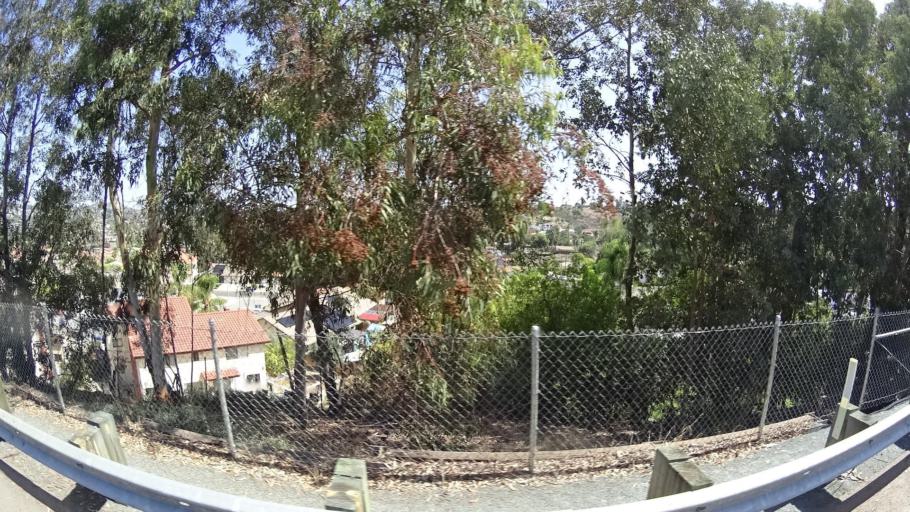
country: US
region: California
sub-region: San Diego County
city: Spring Valley
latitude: 32.7416
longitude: -116.9920
